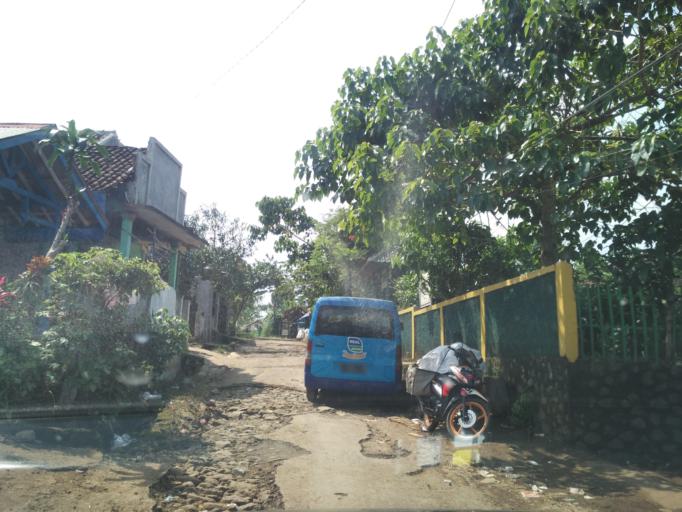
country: ID
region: West Java
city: Sukabumi
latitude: -6.8231
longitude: 107.0583
